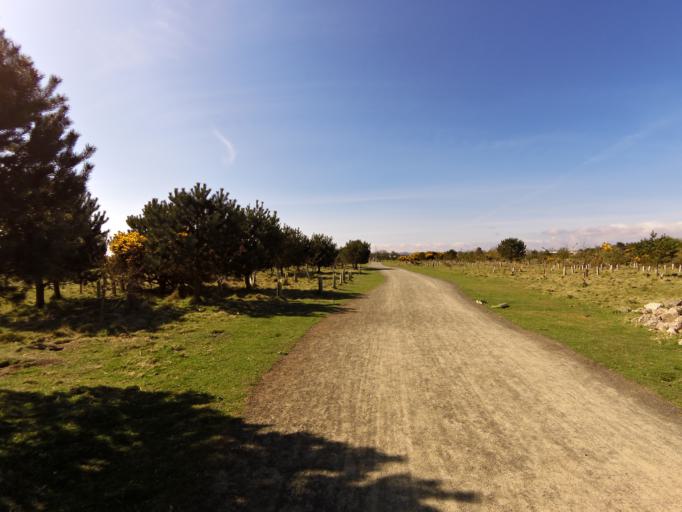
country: GB
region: Scotland
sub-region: Angus
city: Montrose
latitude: 56.7267
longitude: -2.4547
